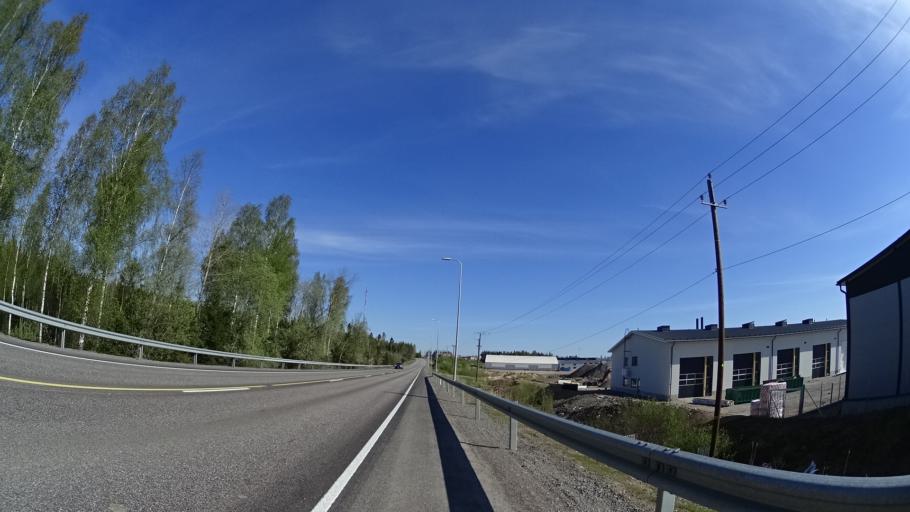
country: FI
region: Uusimaa
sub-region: Helsinki
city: Nurmijaervi
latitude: 60.4464
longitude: 24.8335
